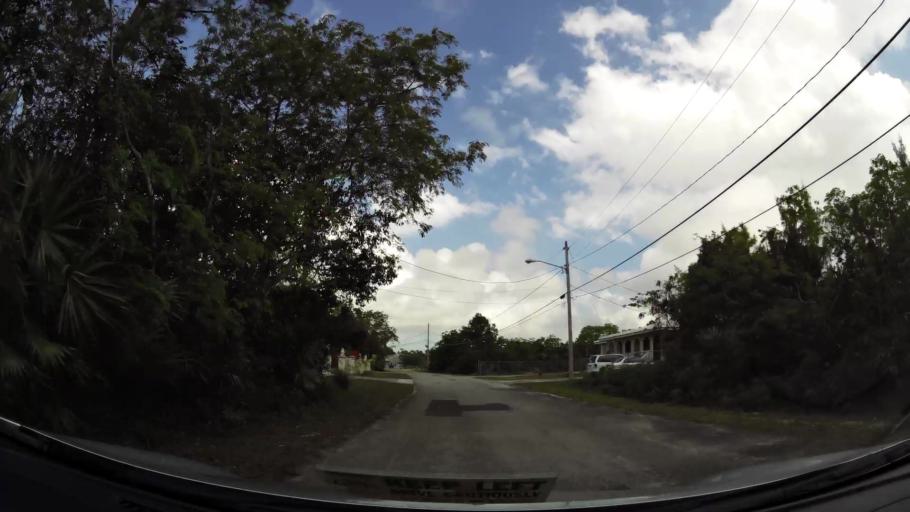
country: BS
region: Freeport
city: Lucaya
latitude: 26.5439
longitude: -78.5883
